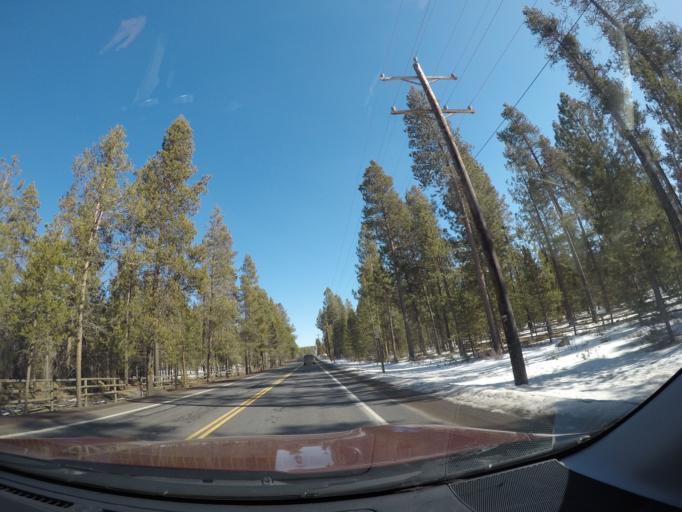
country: US
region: Oregon
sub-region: Deschutes County
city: Sunriver
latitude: 43.8633
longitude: -121.4445
